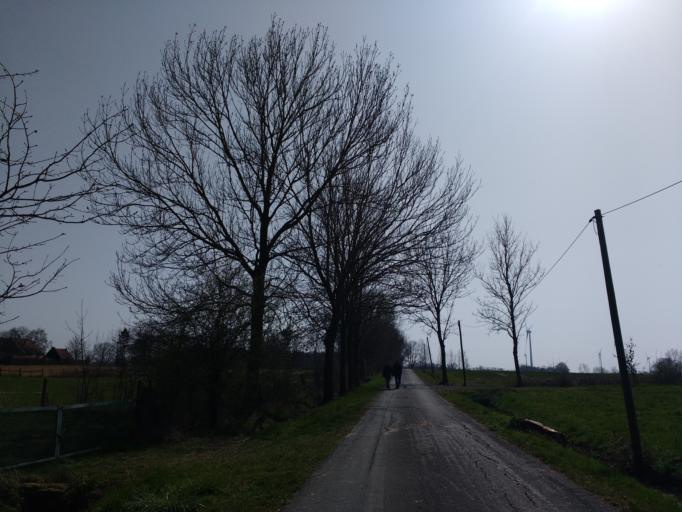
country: DE
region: North Rhine-Westphalia
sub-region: Regierungsbezirk Detmold
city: Salzkotten
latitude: 51.7274
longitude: 8.6516
